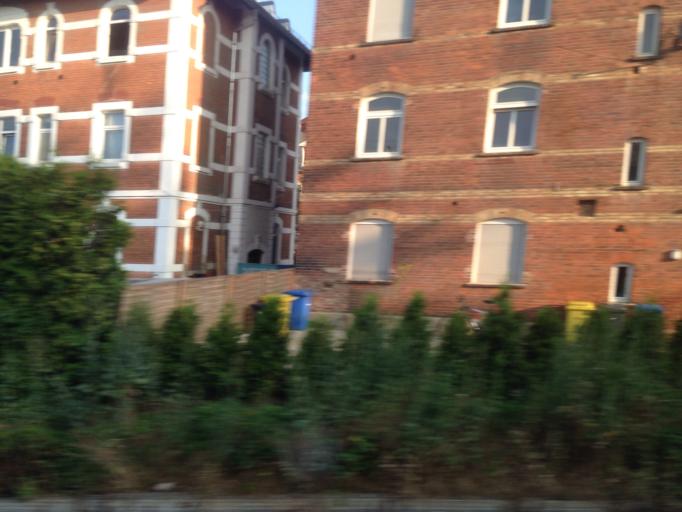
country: DE
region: Thuringia
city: Jena
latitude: 50.9156
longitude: 11.5780
